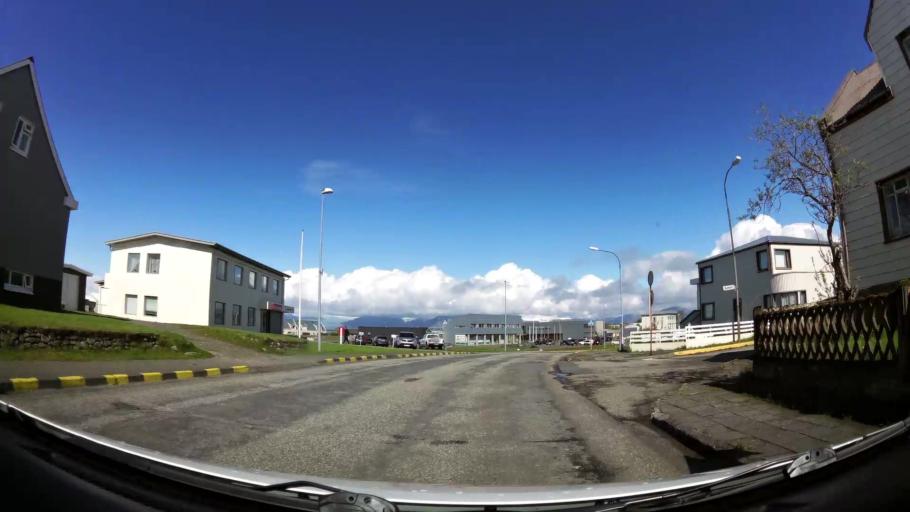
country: IS
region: East
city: Hoefn
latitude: 64.2515
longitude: -15.2103
